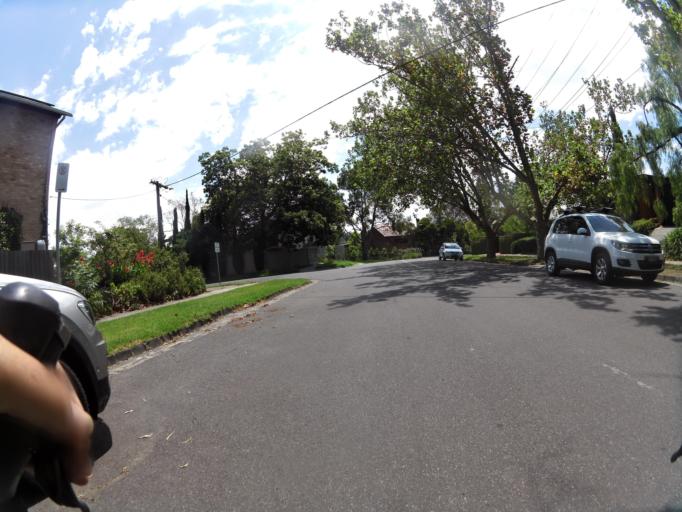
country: AU
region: Victoria
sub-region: Boroondara
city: Kew
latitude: -37.8050
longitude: 145.0206
